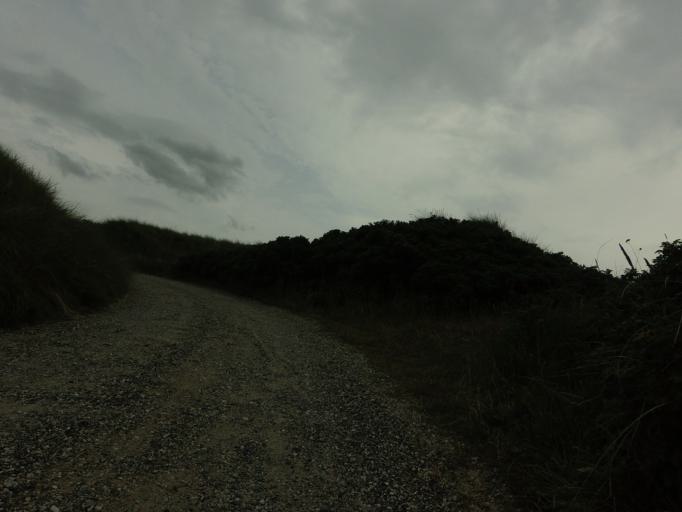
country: DK
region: North Denmark
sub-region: Jammerbugt Kommune
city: Pandrup
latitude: 57.3045
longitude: 9.6446
